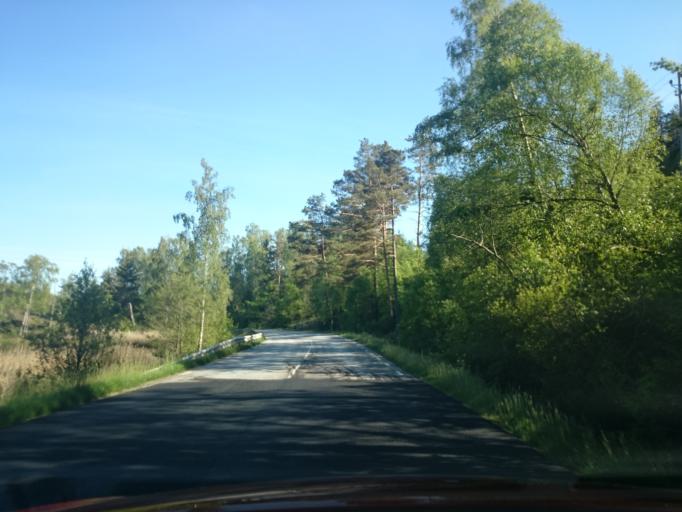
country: SE
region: Vaestra Goetaland
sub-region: Lysekils Kommun
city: Lysekil
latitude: 58.2730
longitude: 11.5323
